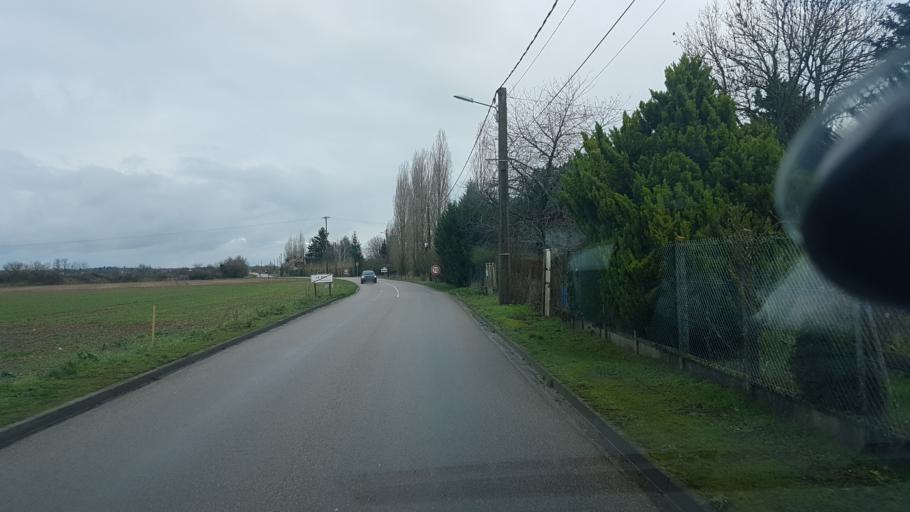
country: FR
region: Ile-de-France
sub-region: Departement de Seine-et-Marne
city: Souppes-sur-Loing
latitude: 48.2064
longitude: 2.7828
